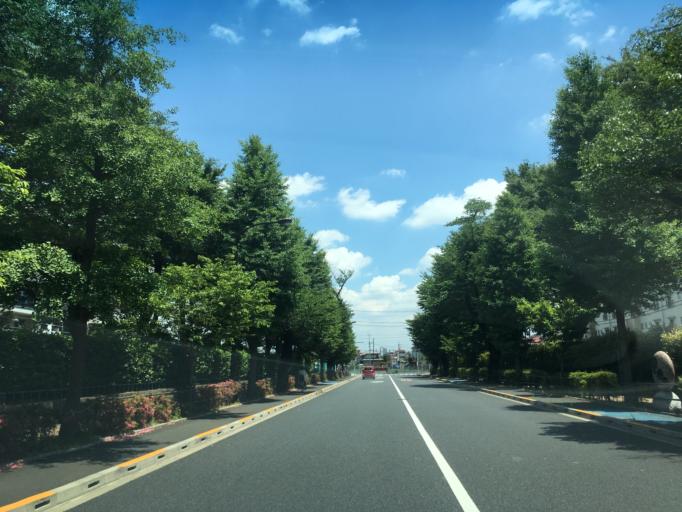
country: JP
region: Tokyo
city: Kokubunji
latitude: 35.6854
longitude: 139.4507
